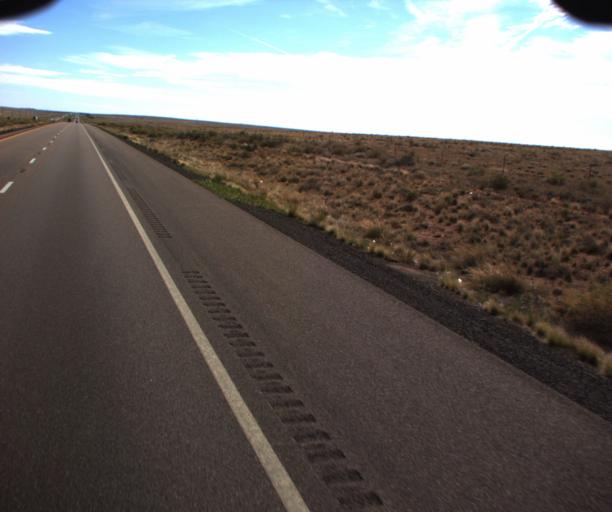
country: US
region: Arizona
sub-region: Navajo County
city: Holbrook
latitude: 35.0243
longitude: -109.8437
